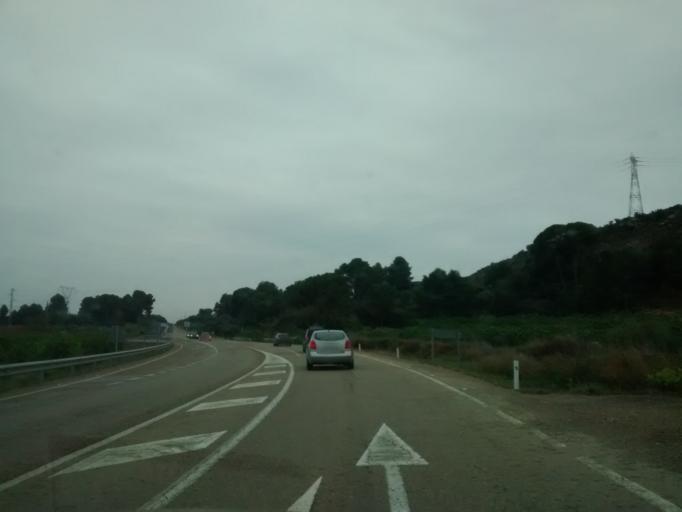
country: ES
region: Aragon
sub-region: Provincia de Zaragoza
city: Caspe
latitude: 41.2464
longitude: -0.0677
